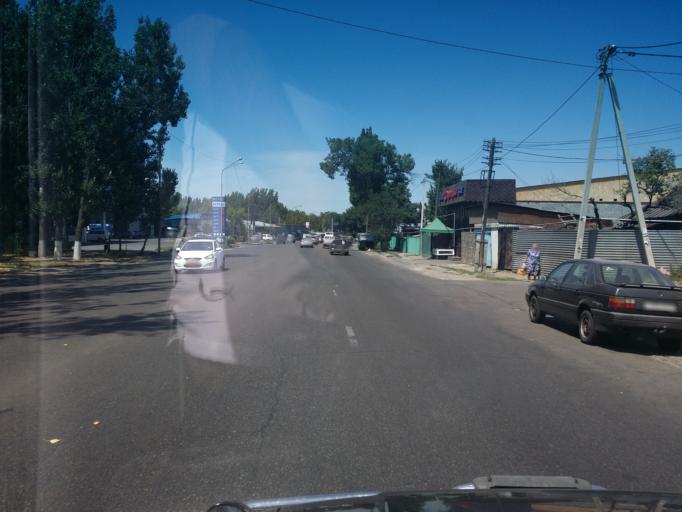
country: KZ
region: Almaty Qalasy
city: Almaty
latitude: 43.2984
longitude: 76.9314
